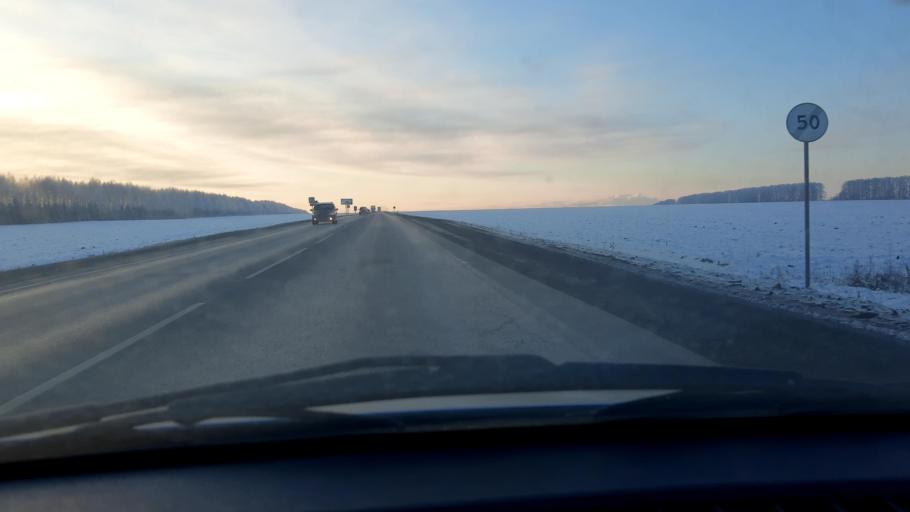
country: RU
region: Bashkortostan
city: Iglino
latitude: 54.7598
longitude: 56.3858
